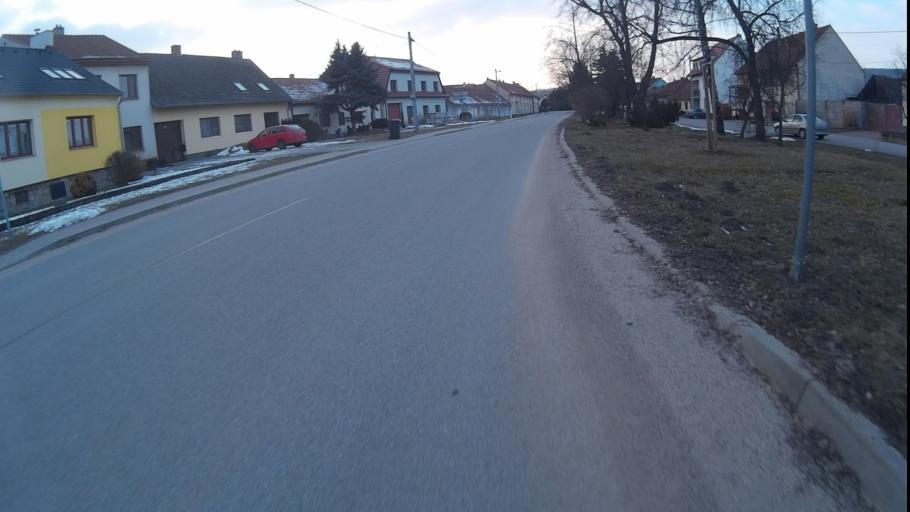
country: CZ
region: South Moravian
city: Vinicne Sumice
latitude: 49.2042
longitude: 16.8219
